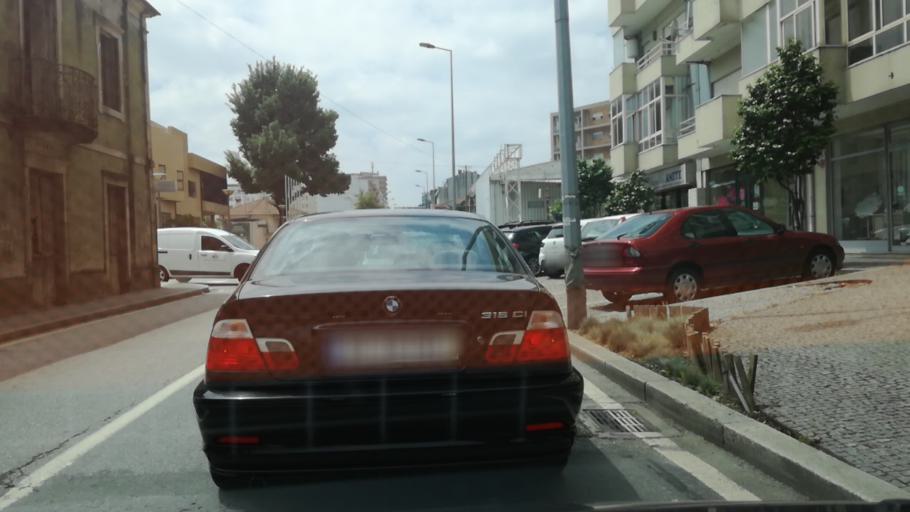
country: PT
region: Porto
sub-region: Trofa
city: Bougado
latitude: 41.3419
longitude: -8.5575
